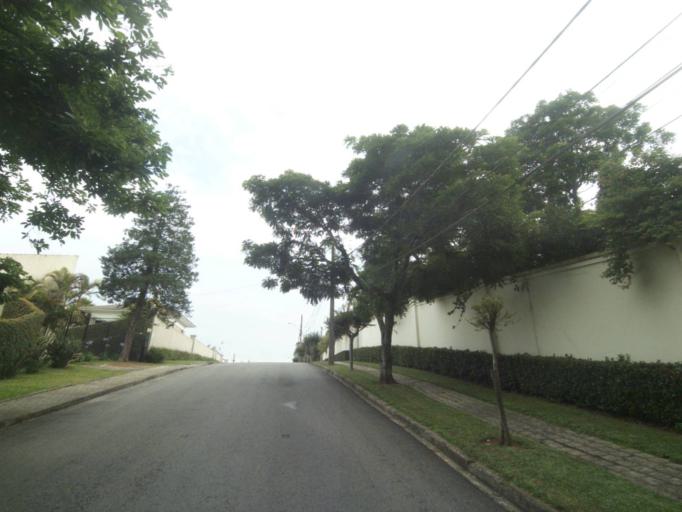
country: BR
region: Parana
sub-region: Curitiba
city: Curitiba
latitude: -25.4072
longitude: -49.3113
